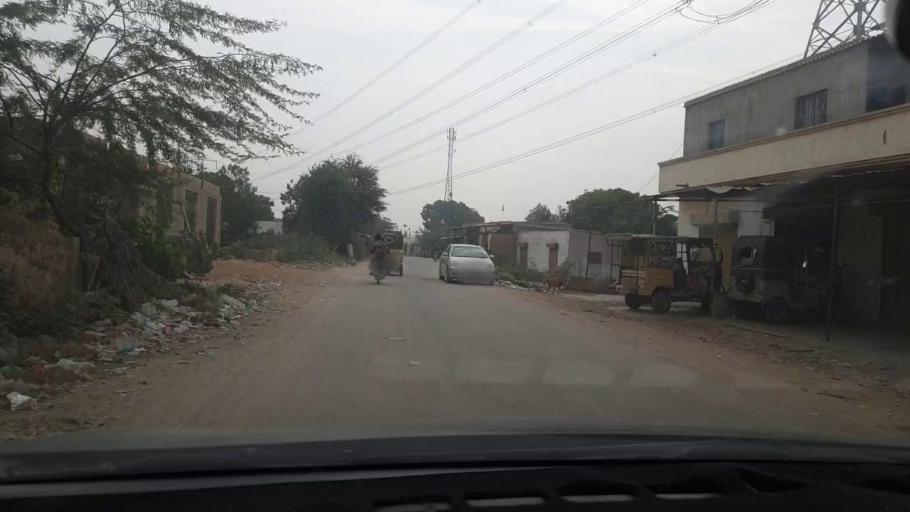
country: PK
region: Sindh
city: Malir Cantonment
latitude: 24.9083
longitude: 67.2856
